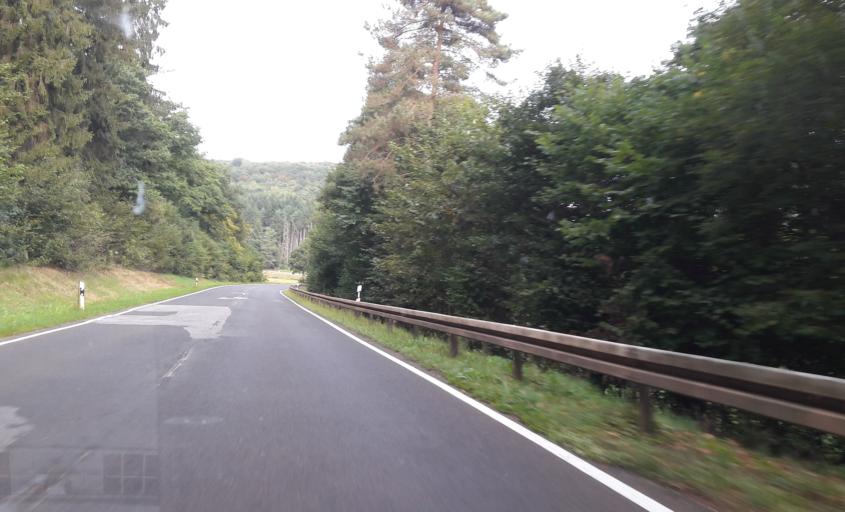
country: DE
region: Rheinland-Pfalz
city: Ellweiler
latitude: 49.6122
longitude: 7.1642
